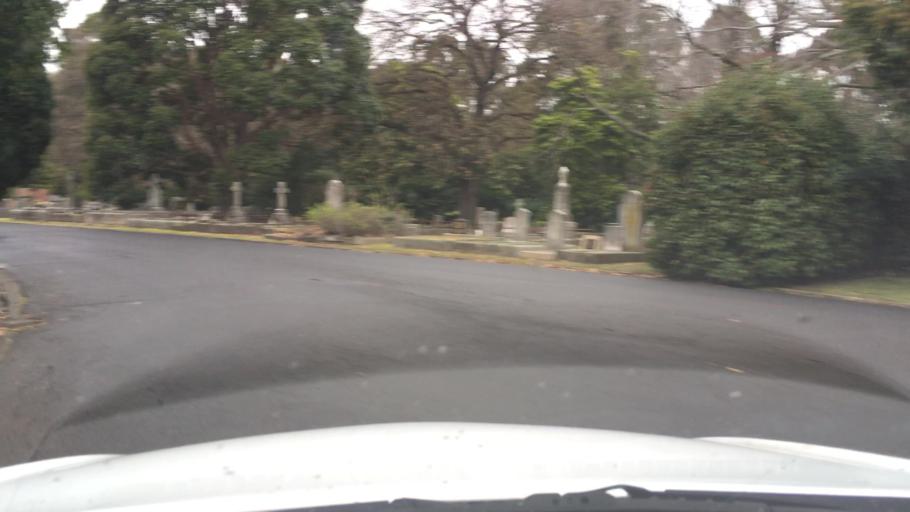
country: AU
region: Victoria
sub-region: Greater Dandenong
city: Noble Park North
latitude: -37.9449
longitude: 145.1790
